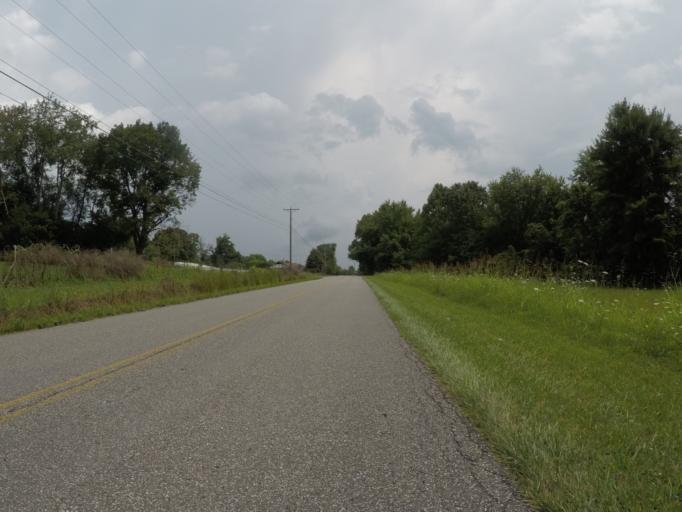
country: US
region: Kentucky
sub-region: Boyd County
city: Meads
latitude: 38.4370
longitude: -82.7082
